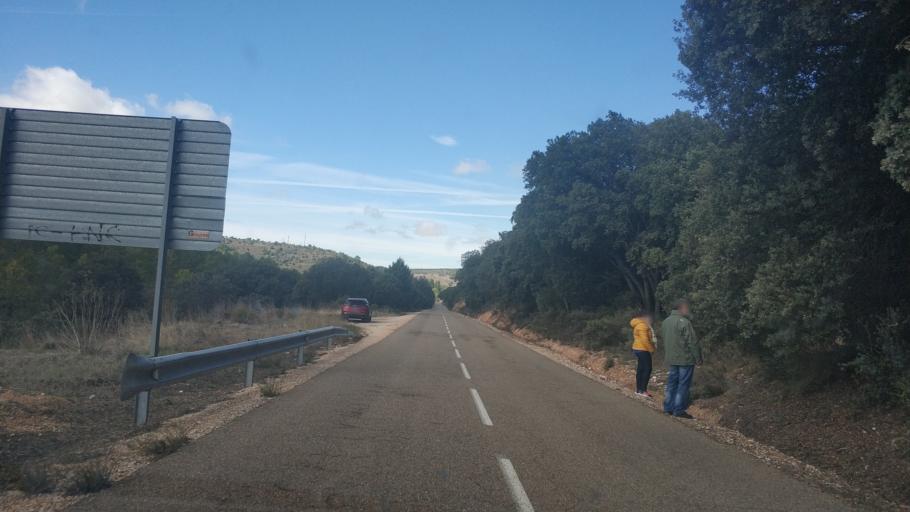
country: ES
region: Castille and Leon
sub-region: Provincia de Burgos
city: Covarrubias
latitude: 42.0520
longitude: -3.4971
